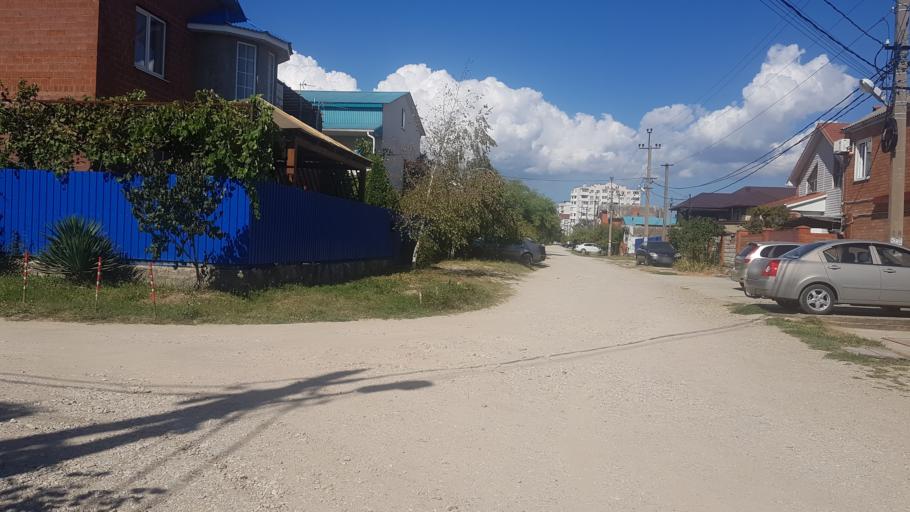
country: RU
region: Krasnodarskiy
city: Arkhipo-Osipovka
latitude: 44.3680
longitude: 38.5254
